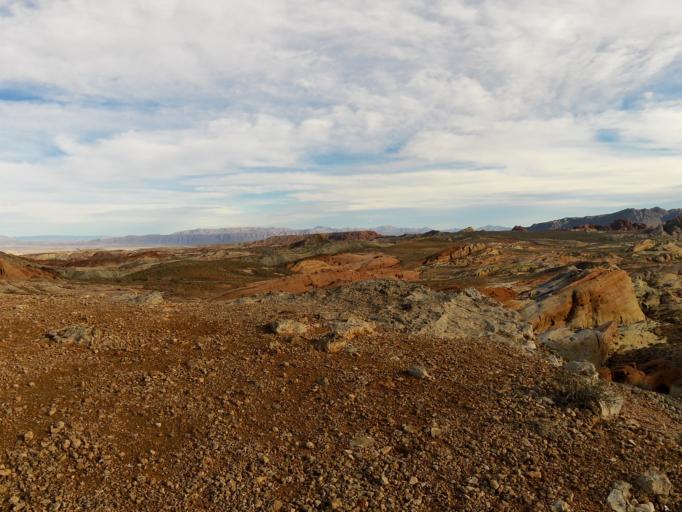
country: US
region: Nevada
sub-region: Clark County
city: Moapa Valley
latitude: 36.4872
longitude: -114.5310
